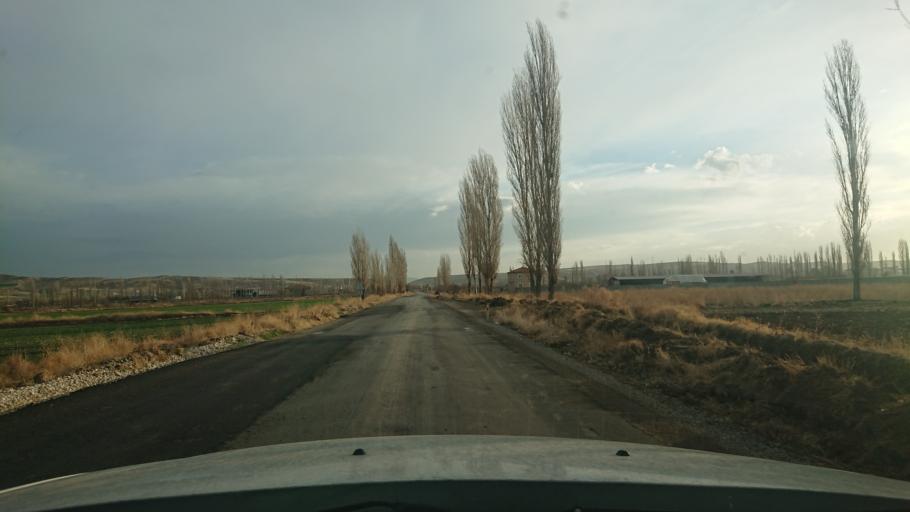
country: TR
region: Aksaray
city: Acipinar
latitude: 38.4795
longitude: 33.8859
